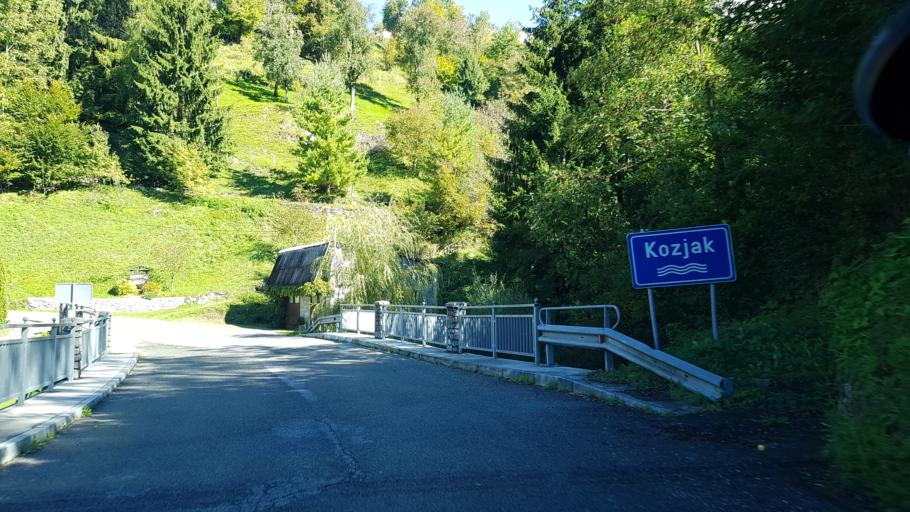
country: SI
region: Kobarid
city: Kobarid
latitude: 46.2668
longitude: 13.6106
